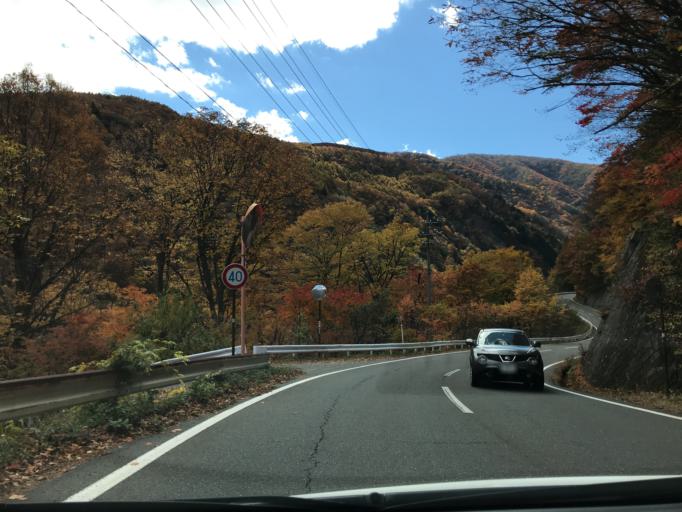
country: JP
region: Nagano
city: Toyoshina
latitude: 36.1344
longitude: 137.6722
